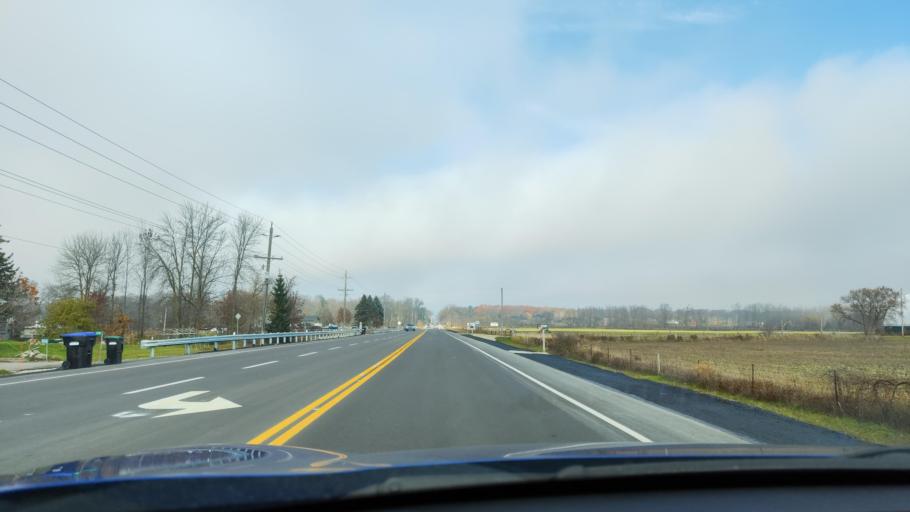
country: CA
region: Ontario
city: Wasaga Beach
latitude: 44.4571
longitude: -80.0718
